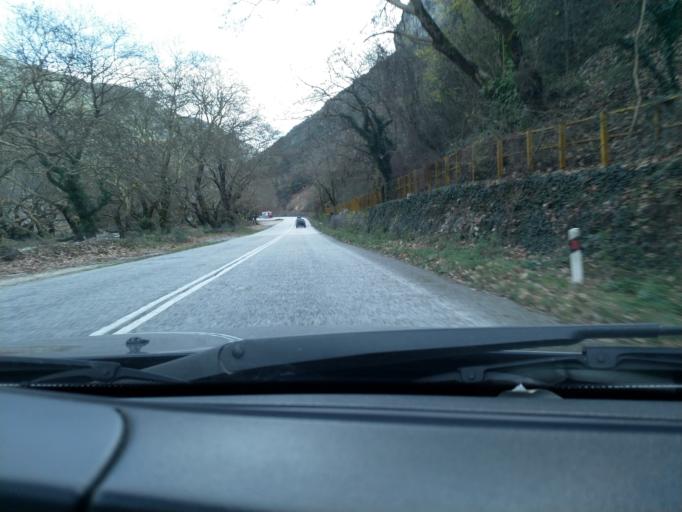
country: GR
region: Epirus
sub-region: Nomos Prevezis
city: Pappadates
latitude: 39.3970
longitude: 20.8427
